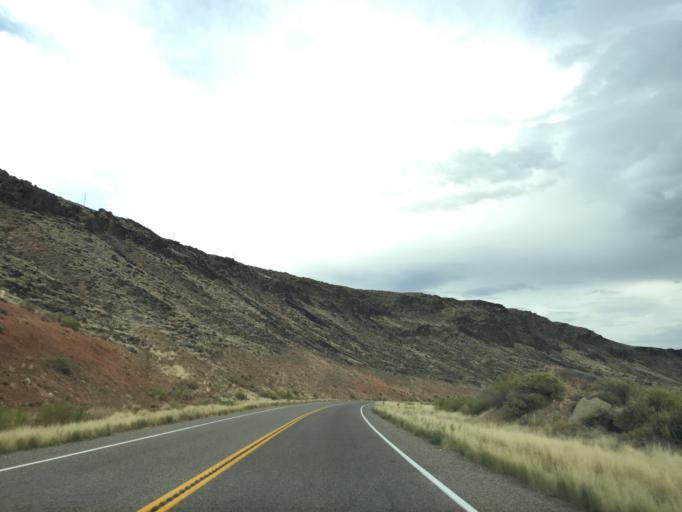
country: US
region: Utah
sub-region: Washington County
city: LaVerkin
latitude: 37.1952
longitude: -113.1510
